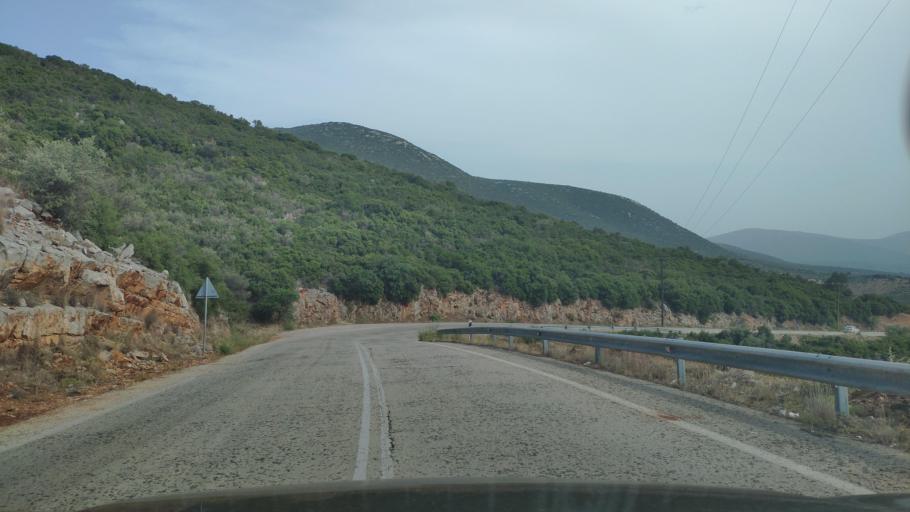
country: GR
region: Peloponnese
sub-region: Nomos Argolidos
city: Palaia Epidavros
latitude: 37.5989
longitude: 23.1570
